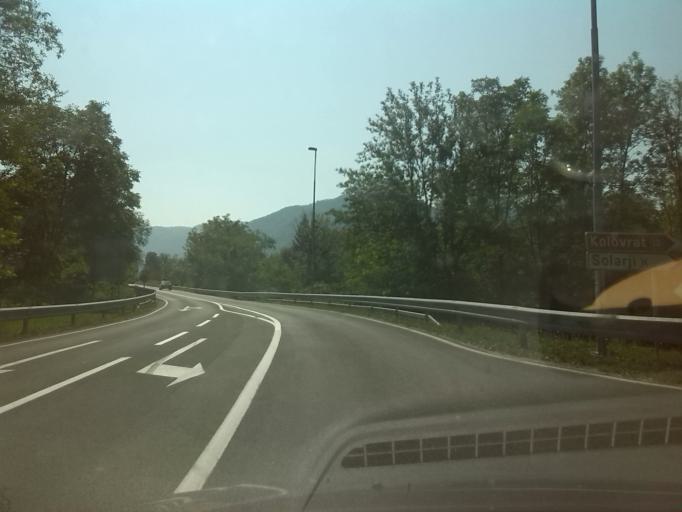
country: SI
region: Tolmin
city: Tolmin
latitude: 46.1847
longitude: 13.7085
